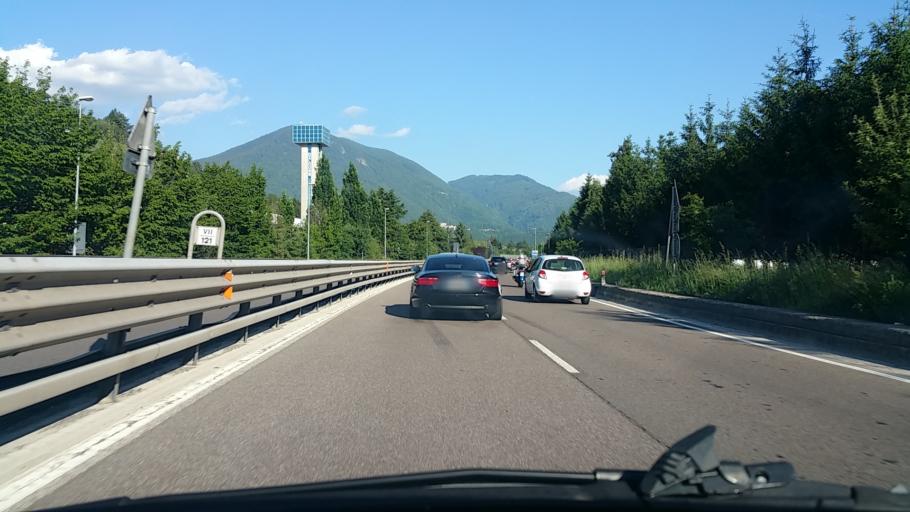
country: IT
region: Trentino-Alto Adige
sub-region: Provincia di Trento
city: Madrano-Canzolino
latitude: 46.0755
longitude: 11.2094
